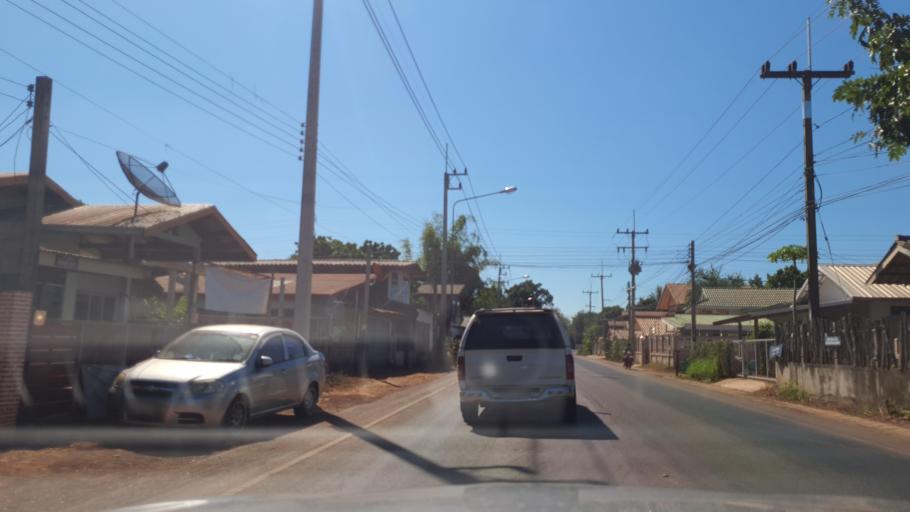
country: TH
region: Sakon Nakhon
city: Phon Na Kaeo
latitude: 17.2661
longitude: 104.1916
